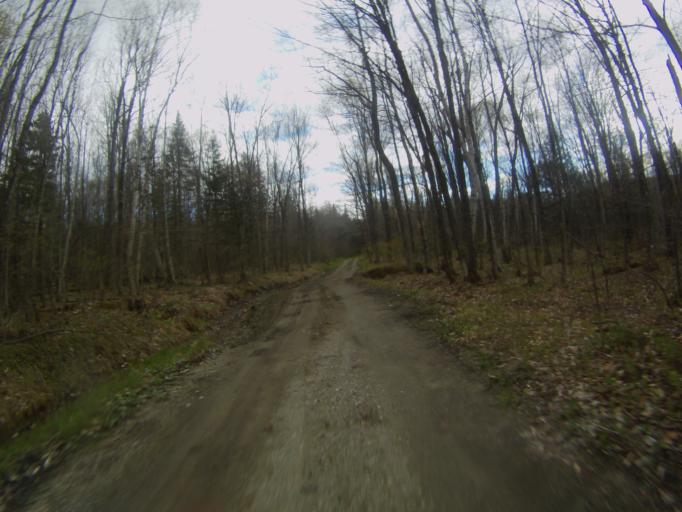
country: US
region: Vermont
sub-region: Addison County
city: Bristol
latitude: 44.0557
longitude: -73.0504
